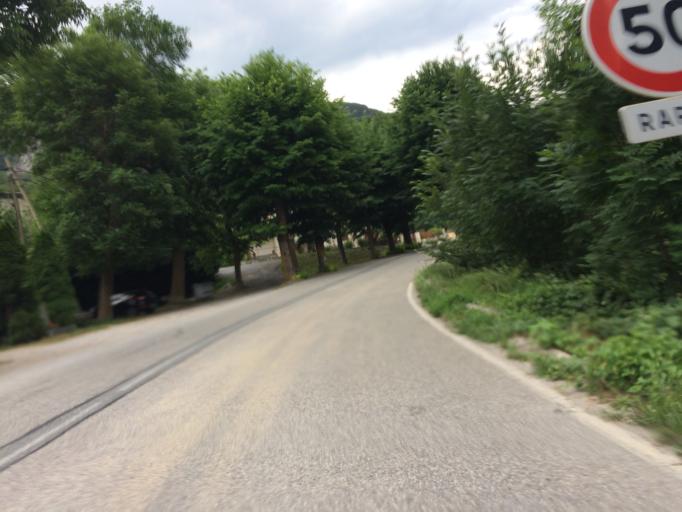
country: FR
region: Provence-Alpes-Cote d'Azur
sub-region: Departement des Alpes-Maritimes
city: Tende
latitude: 44.0792
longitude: 7.5987
